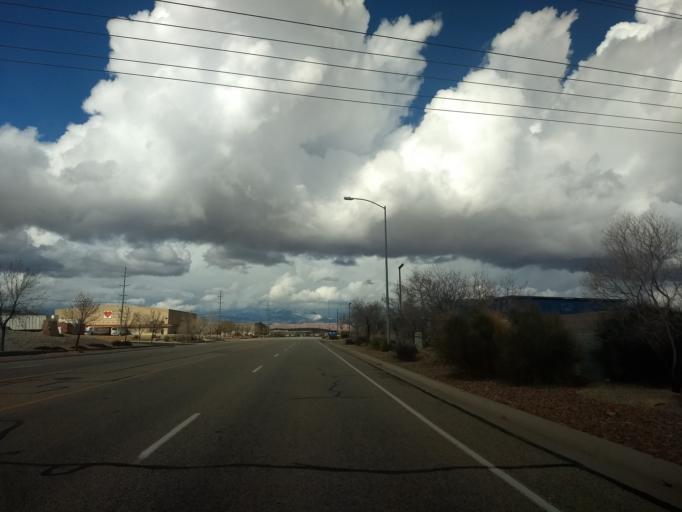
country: US
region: Utah
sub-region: Washington County
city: Saint George
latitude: 37.0304
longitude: -113.5623
